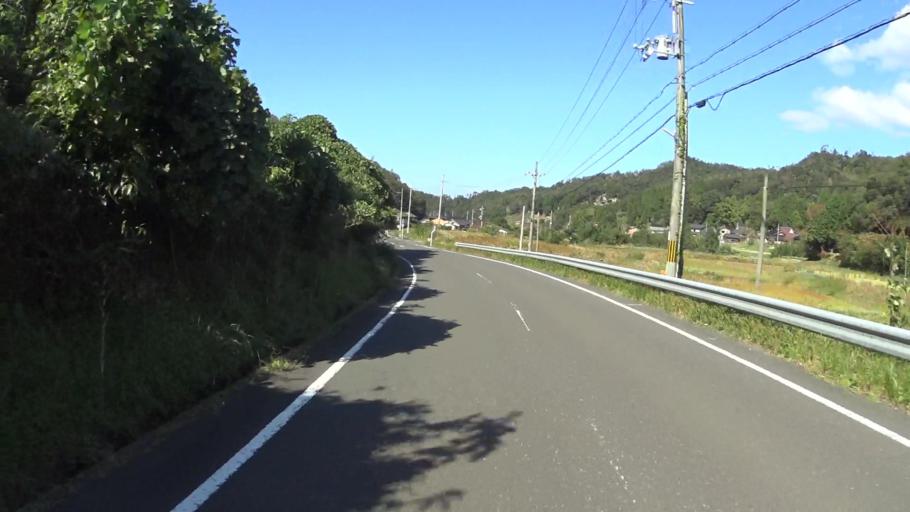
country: JP
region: Hyogo
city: Toyooka
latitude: 35.5598
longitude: 134.9792
